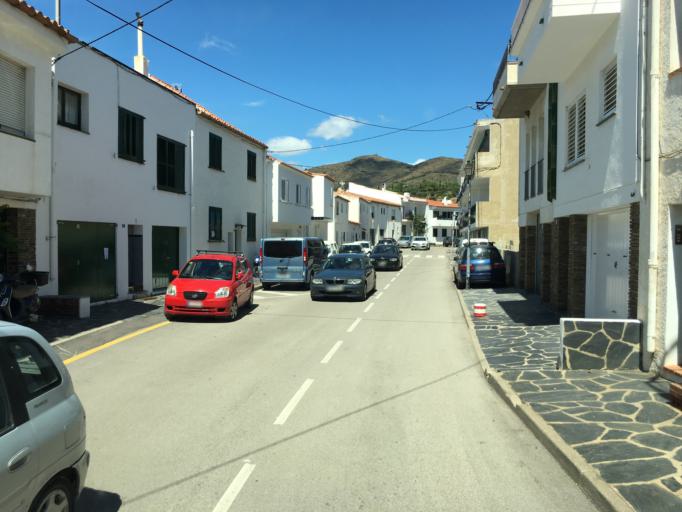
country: ES
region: Catalonia
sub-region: Provincia de Girona
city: Cadaques
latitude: 42.2921
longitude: 3.2795
